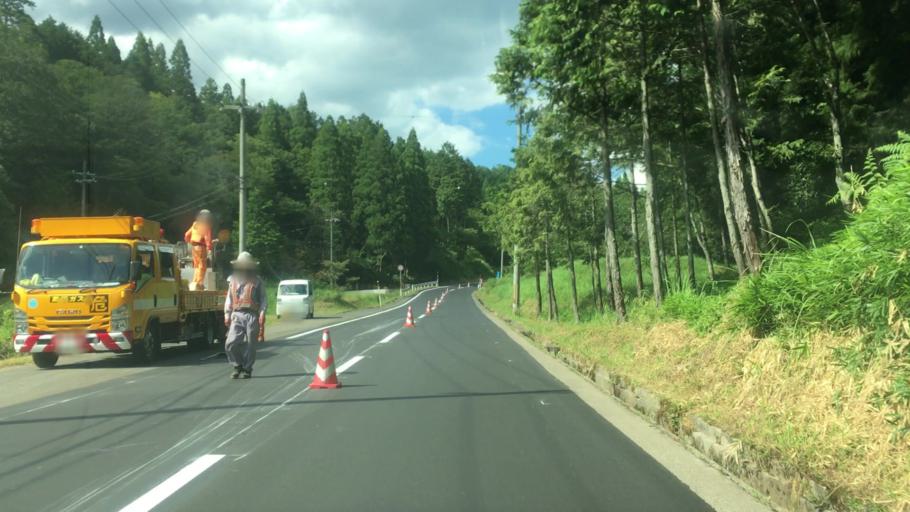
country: JP
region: Hyogo
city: Toyooka
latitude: 35.5057
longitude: 134.7772
